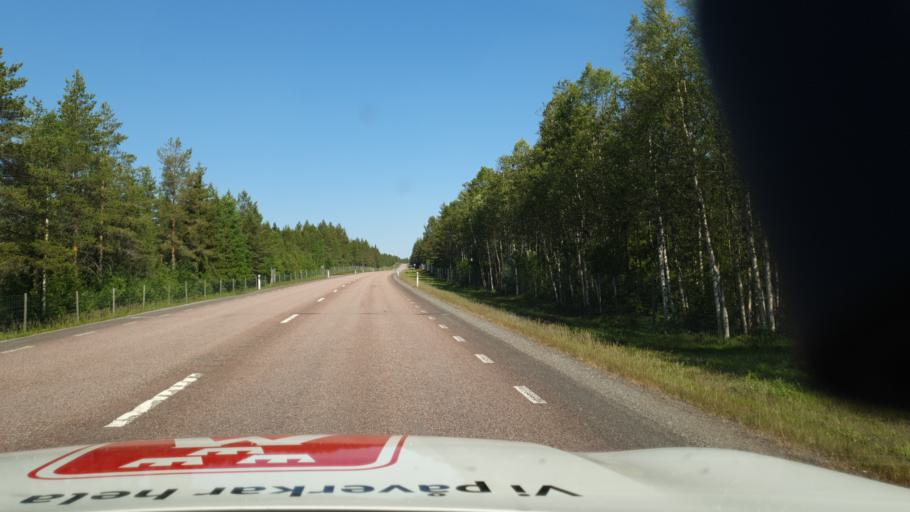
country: SE
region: Vaesterbotten
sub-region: Skelleftea Kommun
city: Burea
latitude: 64.4194
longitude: 21.2877
